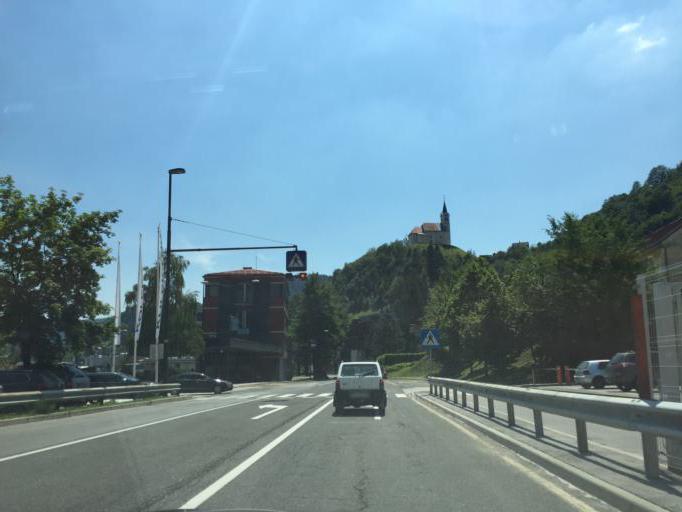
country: SI
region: Idrija
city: Idrija
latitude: 46.0082
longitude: 14.0282
